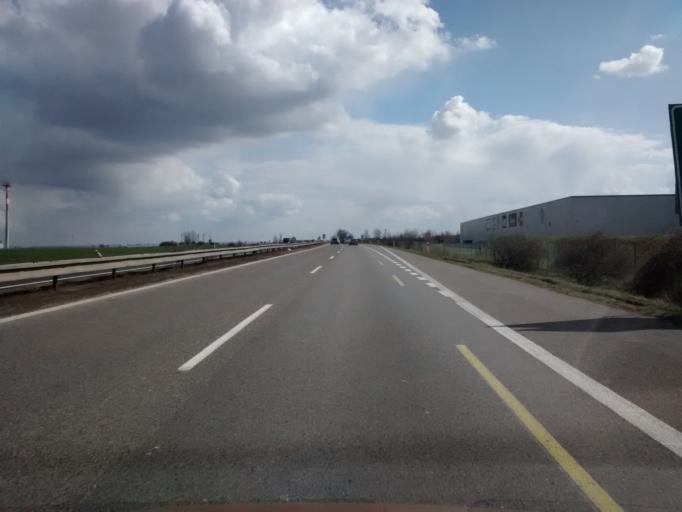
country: CZ
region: Central Bohemia
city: Zdiby
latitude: 50.1795
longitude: 14.4496
